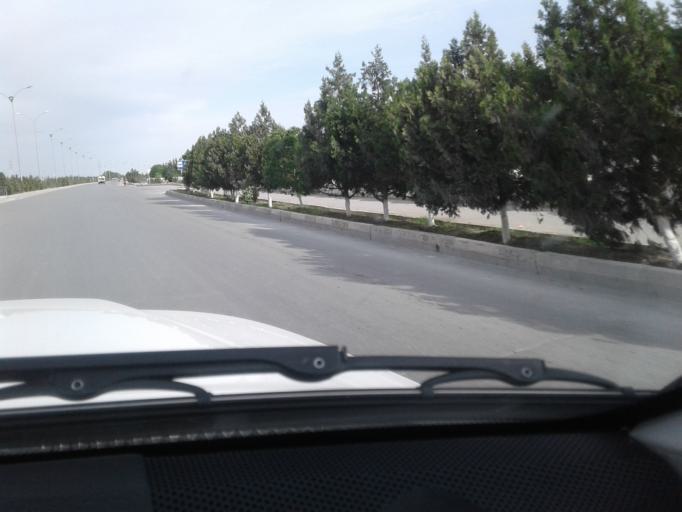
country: TM
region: Ahal
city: Abadan
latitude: 38.1566
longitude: 57.9708
